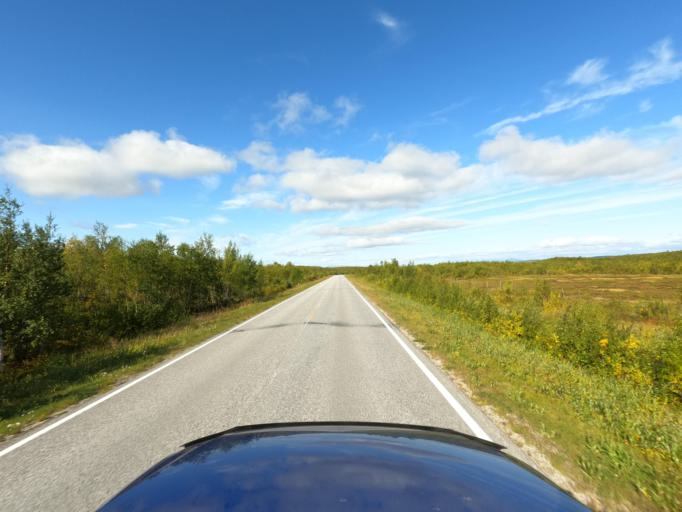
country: NO
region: Finnmark Fylke
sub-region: Karasjok
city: Karasjohka
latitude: 69.5914
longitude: 25.3370
